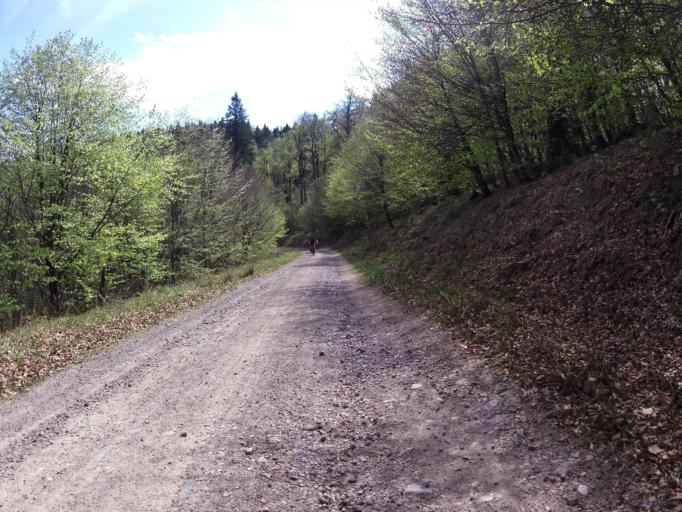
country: DE
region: Thuringia
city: Tabarz
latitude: 50.8392
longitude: 10.4937
